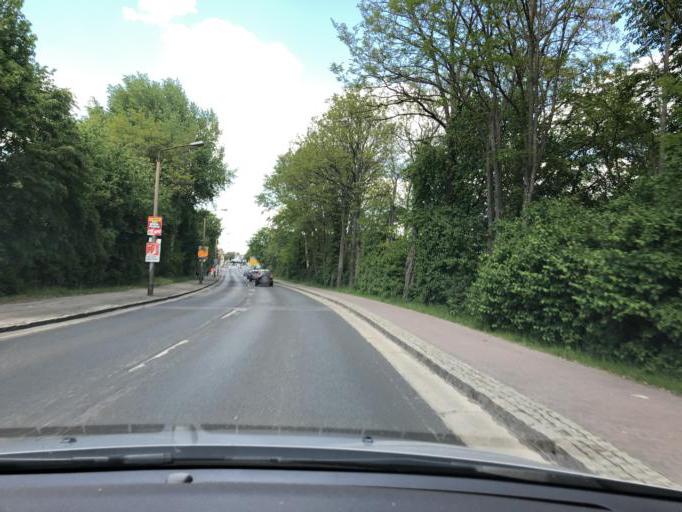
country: DE
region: Brandenburg
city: Storkow
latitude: 52.2576
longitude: 13.9366
